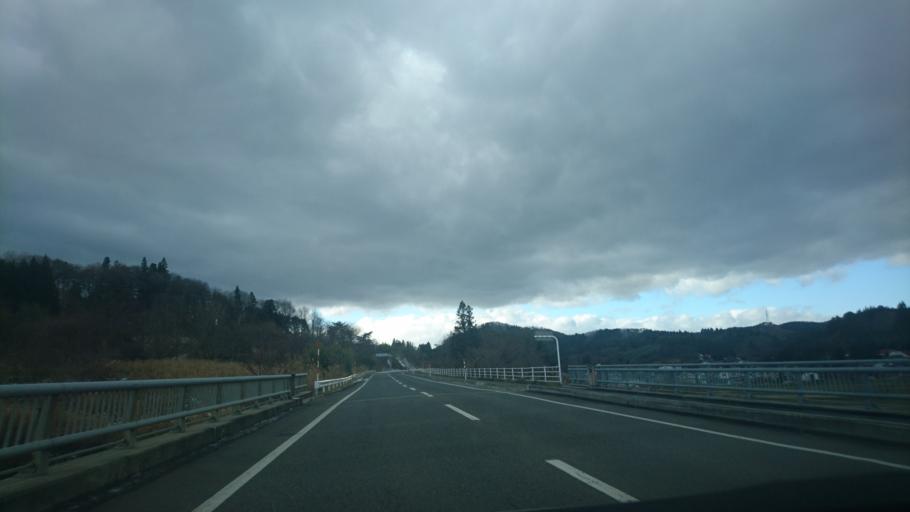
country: JP
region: Iwate
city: Mizusawa
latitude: 39.1797
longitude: 141.3106
